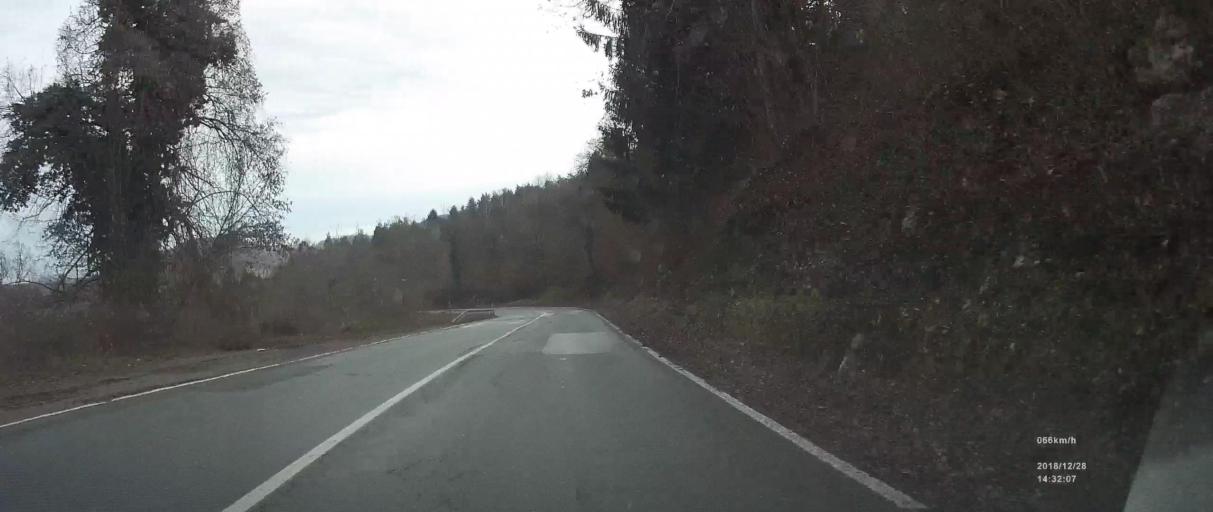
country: HR
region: Primorsko-Goranska
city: Vrbovsko
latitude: 45.4140
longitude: 15.1516
